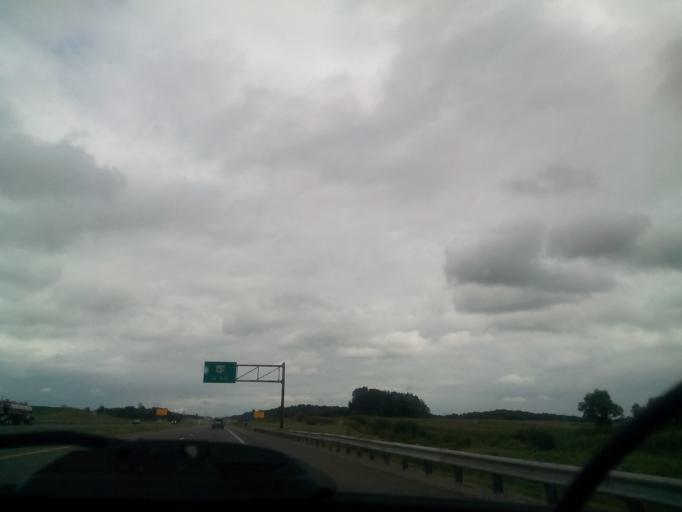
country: US
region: Indiana
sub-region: Steuben County
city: Hamilton
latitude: 41.6305
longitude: -84.7838
